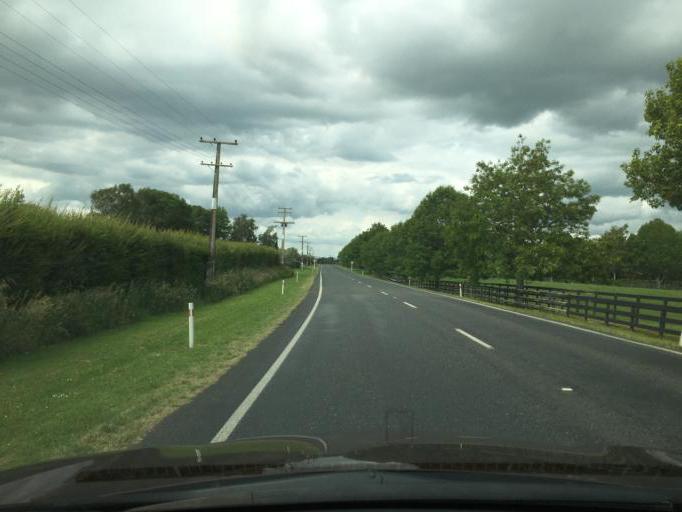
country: NZ
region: Waikato
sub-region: Waipa District
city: Cambridge
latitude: -38.0021
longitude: 175.3900
